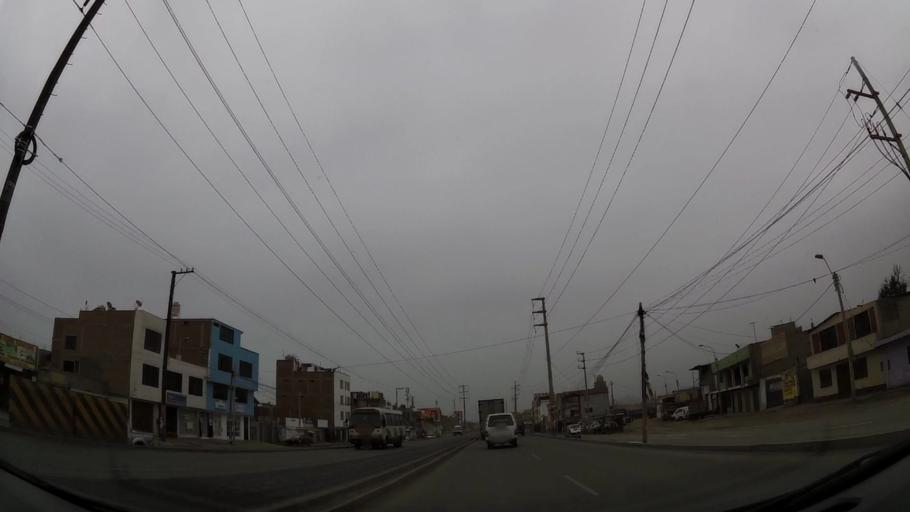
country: PE
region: Lima
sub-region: Lima
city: Punta Hermosa
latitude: -12.2977
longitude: -76.8494
